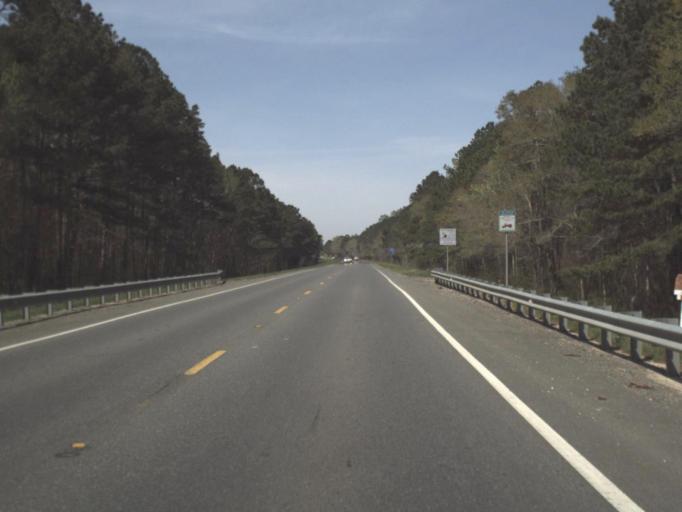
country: US
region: Florida
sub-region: Holmes County
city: Bonifay
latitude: 30.7787
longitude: -85.6164
